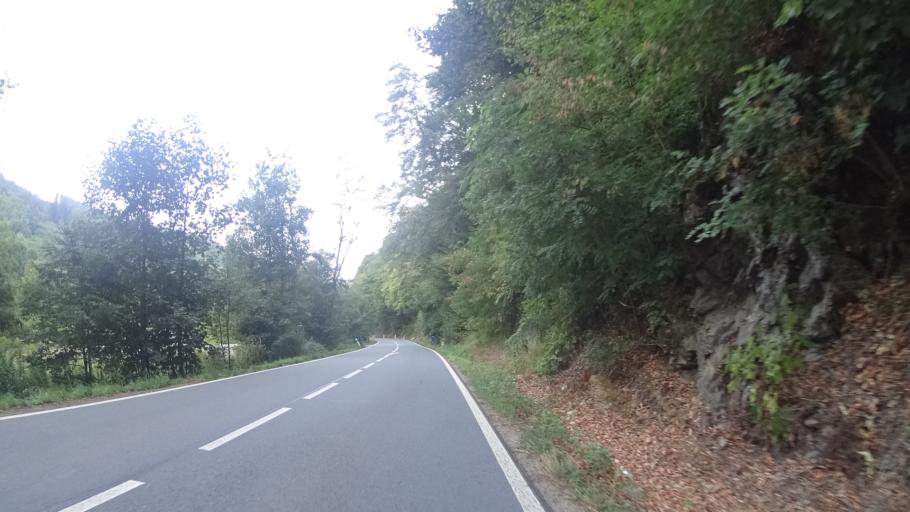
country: CZ
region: Olomoucky
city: Stity
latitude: 49.8721
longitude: 16.7631
